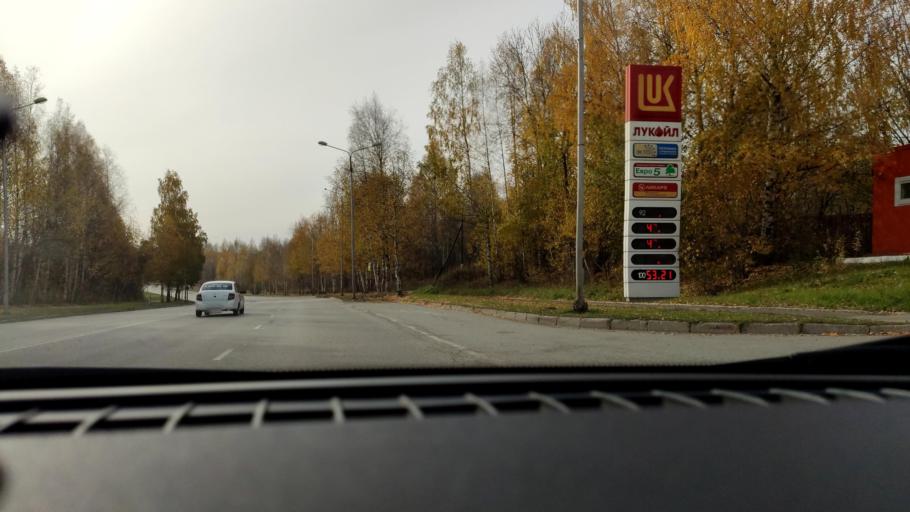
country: RU
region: Perm
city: Perm
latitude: 58.0990
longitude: 56.3869
